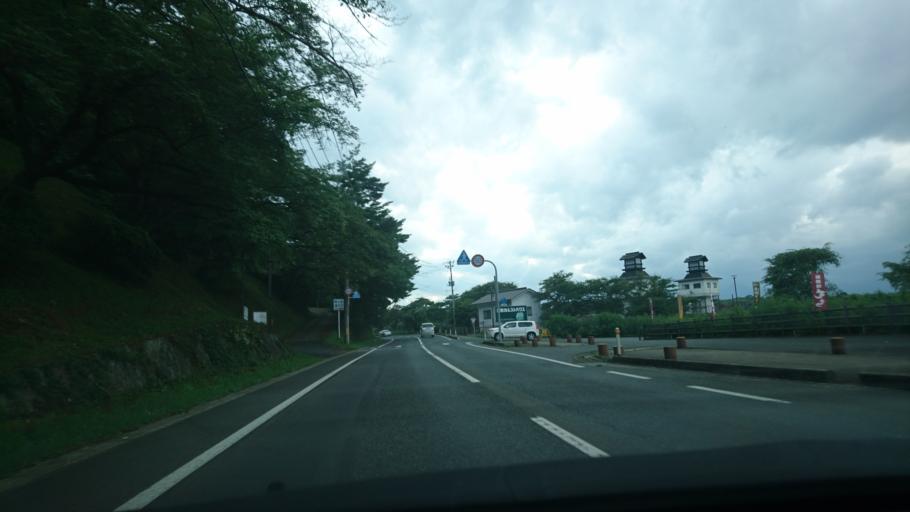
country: JP
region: Iwate
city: Kitakami
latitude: 39.2714
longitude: 141.1267
